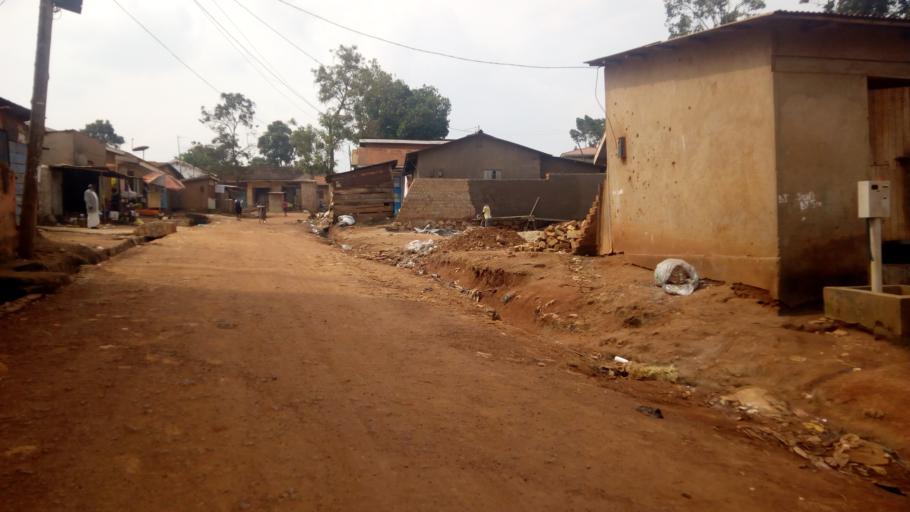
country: UG
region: Central Region
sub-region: Wakiso District
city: Kireka
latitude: 0.3080
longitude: 32.6538
